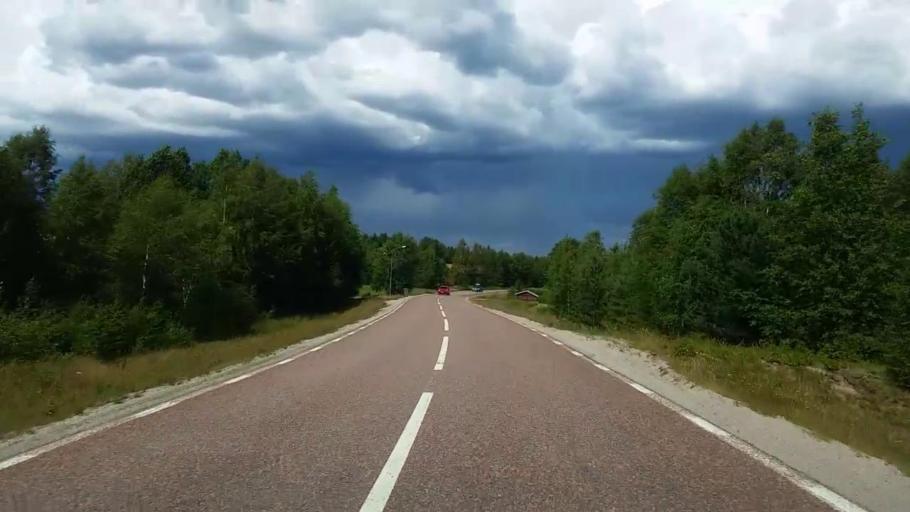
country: SE
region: Gaevleborg
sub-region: Ovanakers Kommun
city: Edsbyn
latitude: 61.3368
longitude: 15.5427
